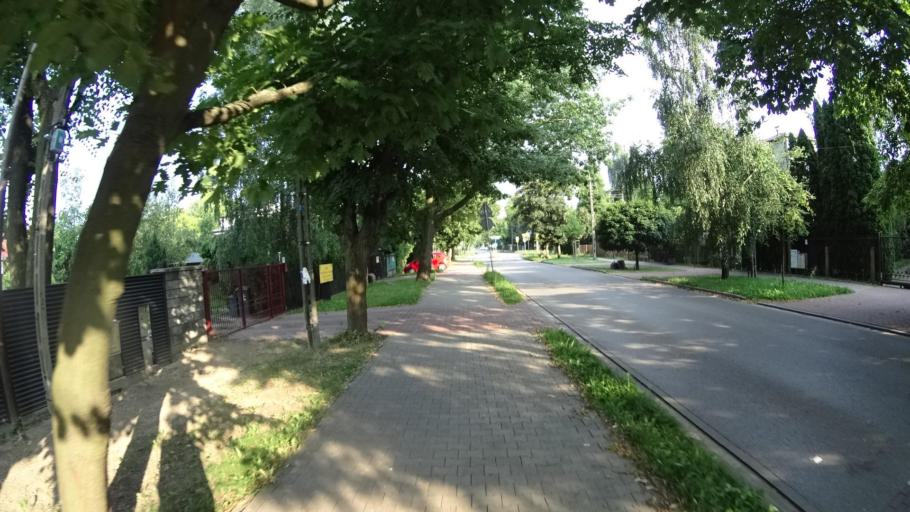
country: PL
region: Masovian Voivodeship
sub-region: Powiat pruszkowski
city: Michalowice
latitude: 52.1694
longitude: 20.8884
